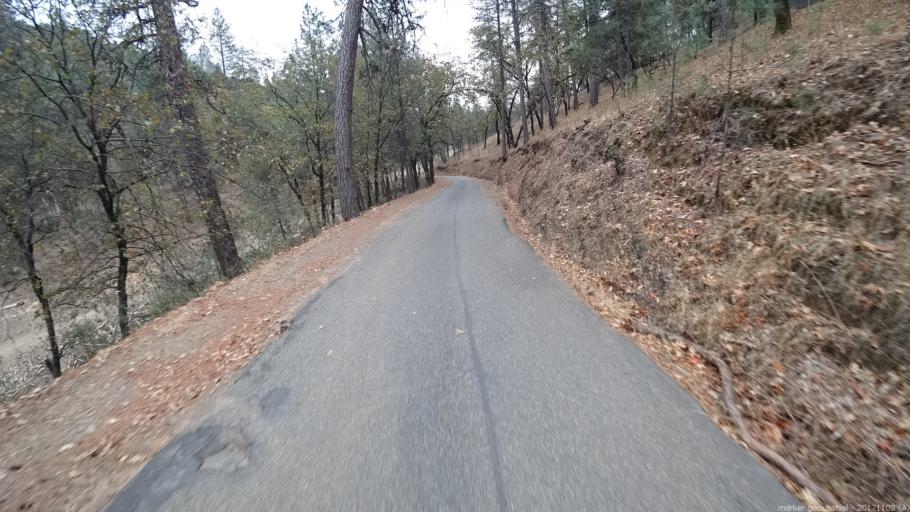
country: US
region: California
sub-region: Shasta County
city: Bella Vista
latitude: 40.7483
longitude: -122.2323
